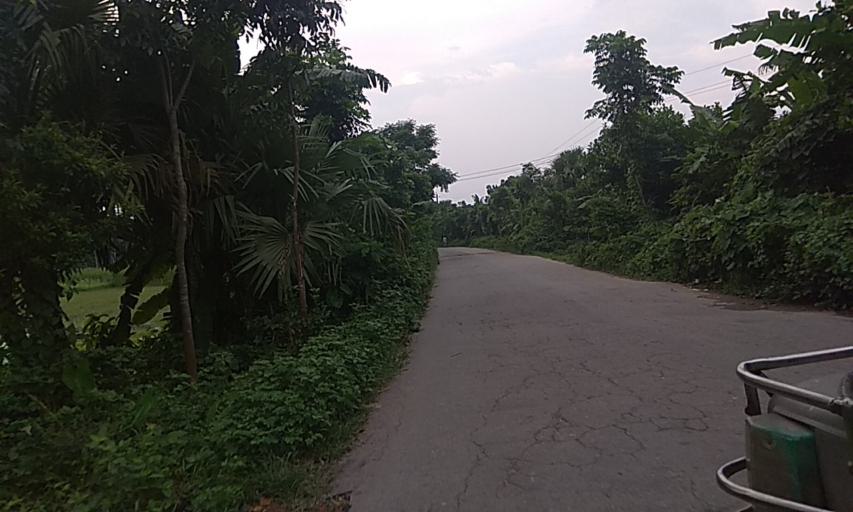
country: BD
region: Dhaka
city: Dohar
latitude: 23.4586
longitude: 89.9995
